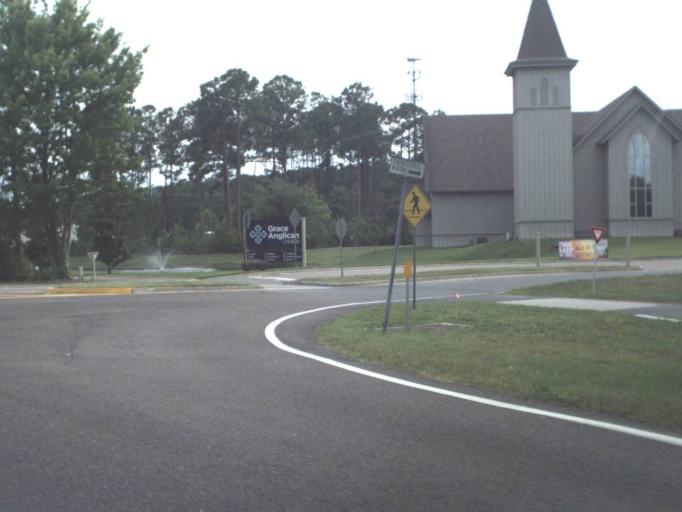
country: US
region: Florida
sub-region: Saint Johns County
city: Fruit Cove
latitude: 30.0924
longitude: -81.7063
